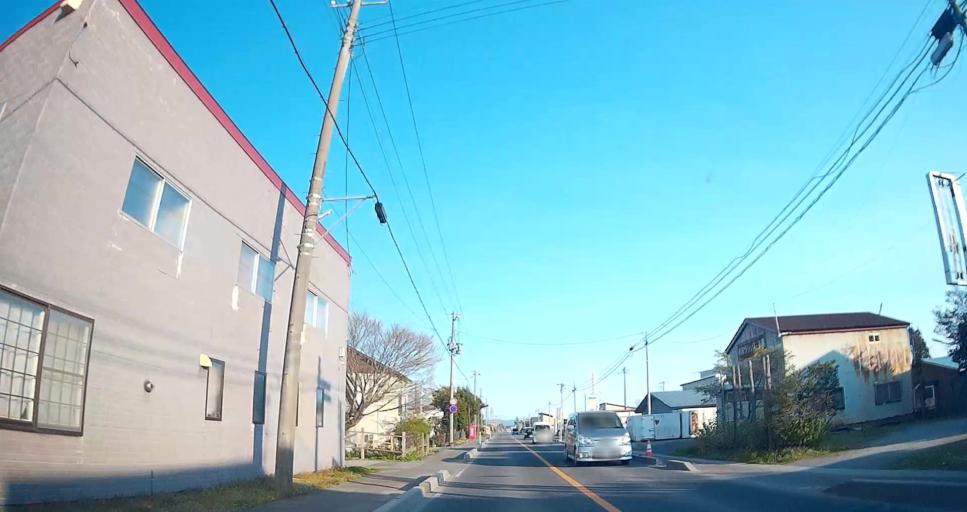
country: JP
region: Aomori
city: Mutsu
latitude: 41.2693
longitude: 141.2194
